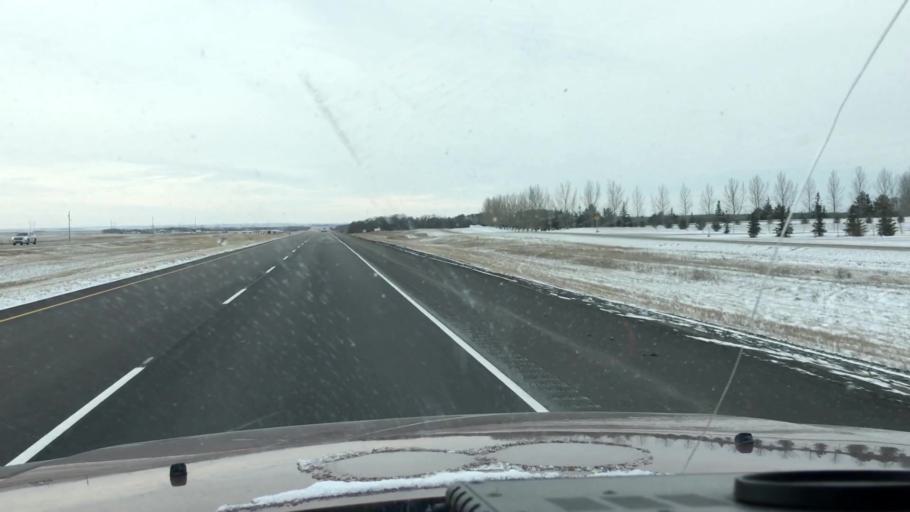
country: CA
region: Saskatchewan
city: Saskatoon
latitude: 51.9071
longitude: -106.5247
